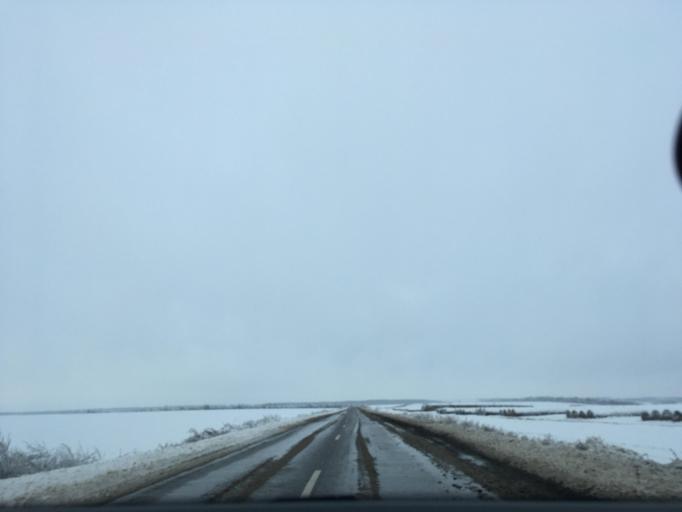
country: RU
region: Voronezj
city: Ol'khovatka
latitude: 50.1311
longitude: 39.1948
